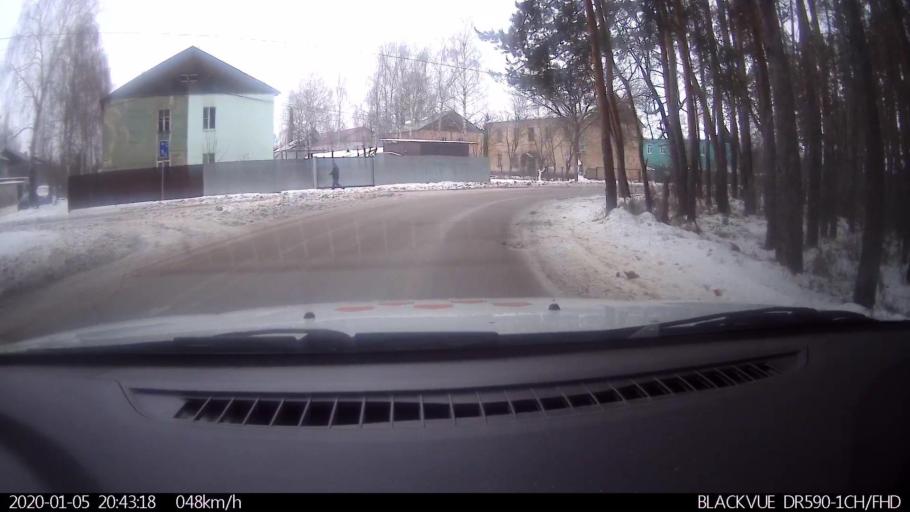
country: RU
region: Nizjnij Novgorod
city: Lukino
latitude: 56.3912
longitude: 43.7395
